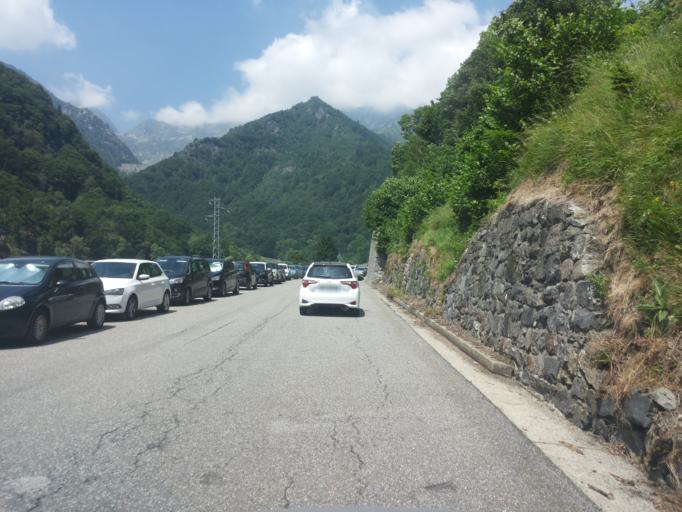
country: IT
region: Piedmont
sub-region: Provincia di Biella
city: Piedicavallo
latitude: 45.6861
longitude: 7.9604
